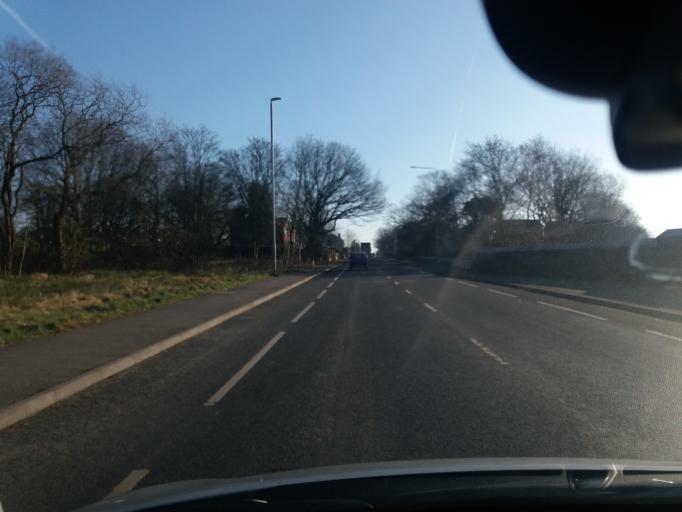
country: GB
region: England
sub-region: Lancashire
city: Adlington
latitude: 53.6278
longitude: -2.6091
